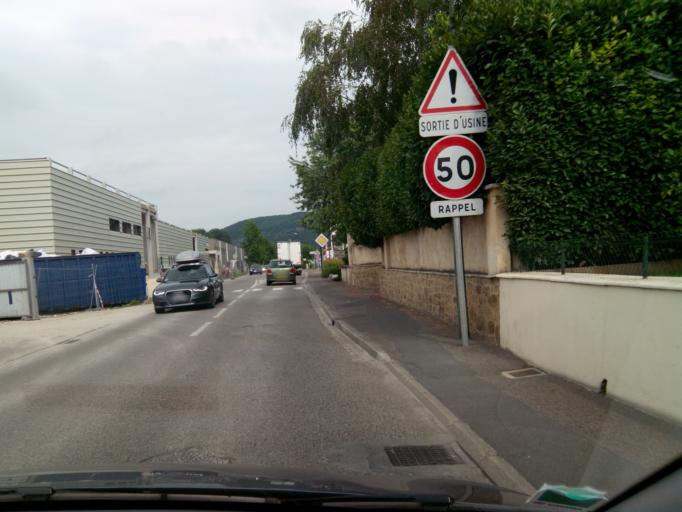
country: FR
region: Midi-Pyrenees
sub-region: Departement du Lot
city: Souillac
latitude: 44.8938
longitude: 1.4701
